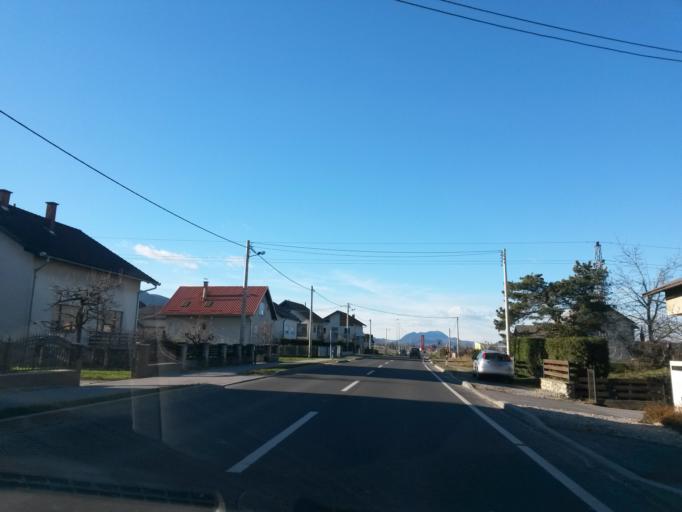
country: HR
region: Varazdinska
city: Ivanec
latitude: 46.2335
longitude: 16.1485
